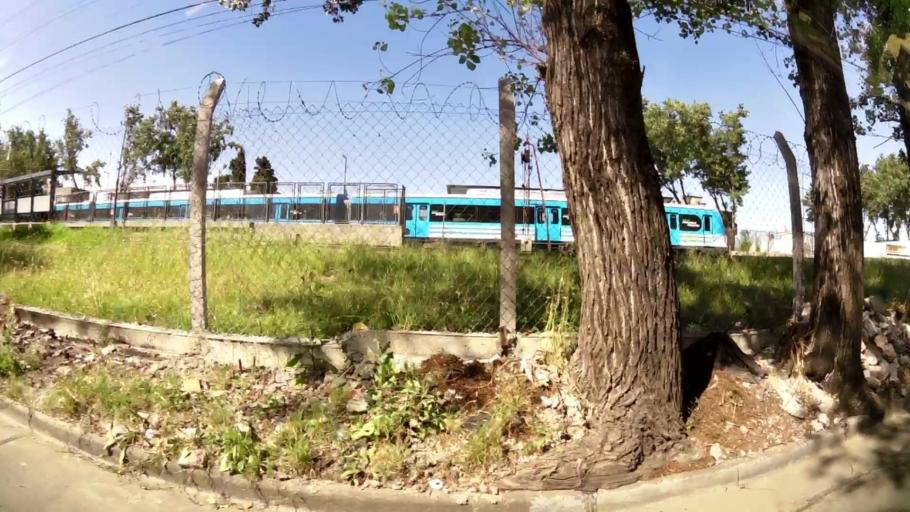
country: AR
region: Buenos Aires
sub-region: Partido de General San Martin
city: General San Martin
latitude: -34.5353
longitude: -58.5757
